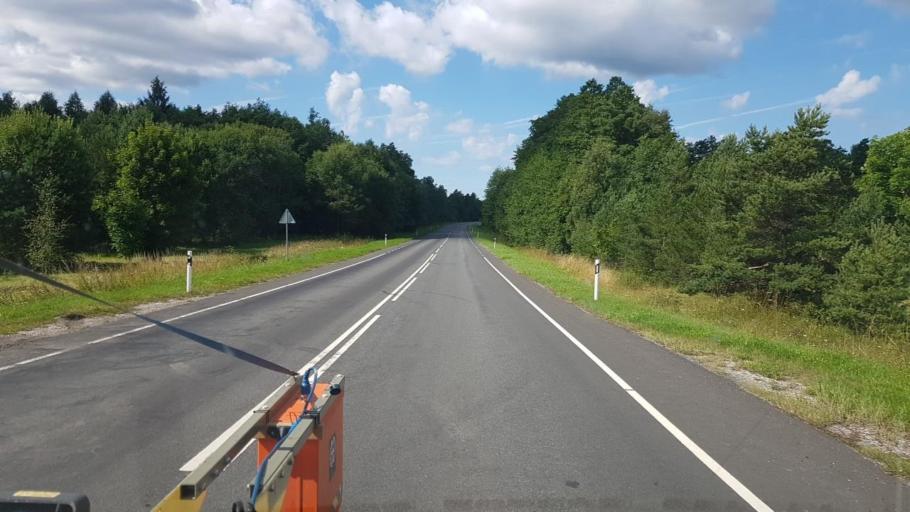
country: EE
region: Hiiumaa
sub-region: Kaerdla linn
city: Kardla
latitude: 58.9897
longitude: 22.7856
